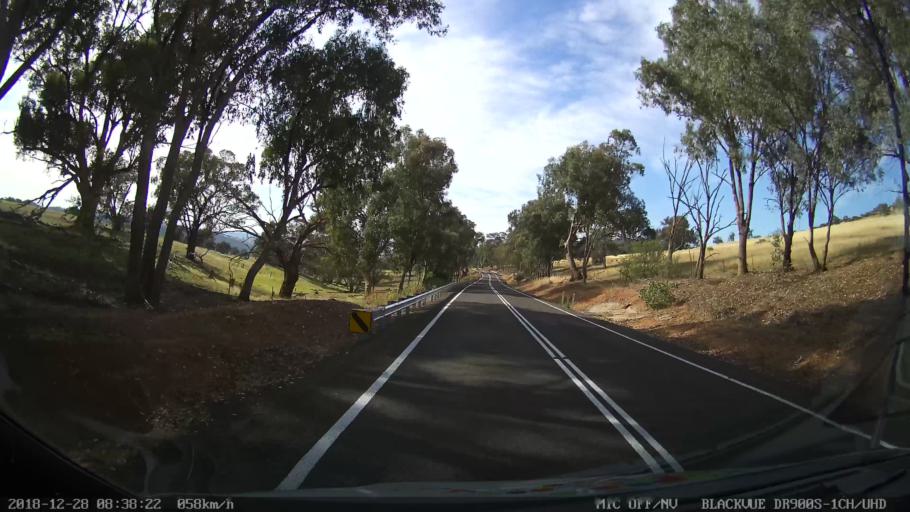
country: AU
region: New South Wales
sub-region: Blayney
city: Blayney
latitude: -34.0031
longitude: 149.3150
